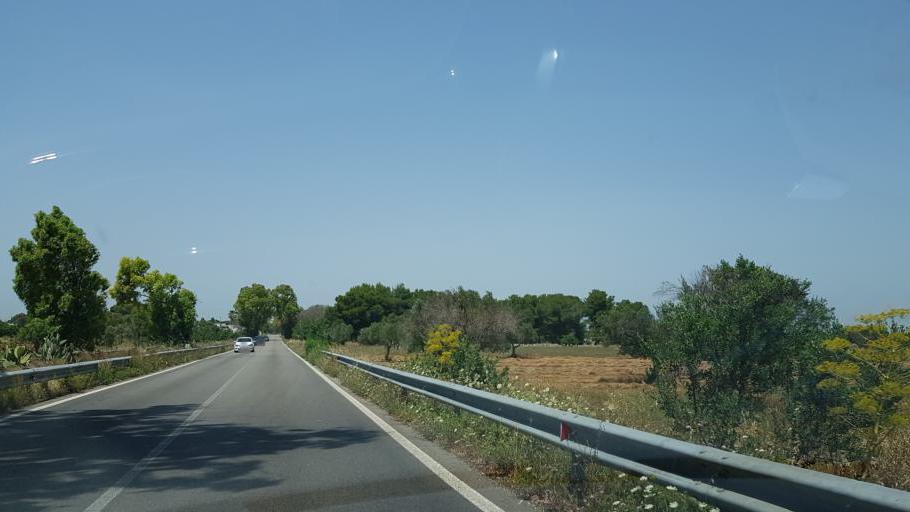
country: IT
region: Apulia
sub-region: Provincia di Lecce
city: Porto Cesareo
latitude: 40.2549
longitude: 17.9291
